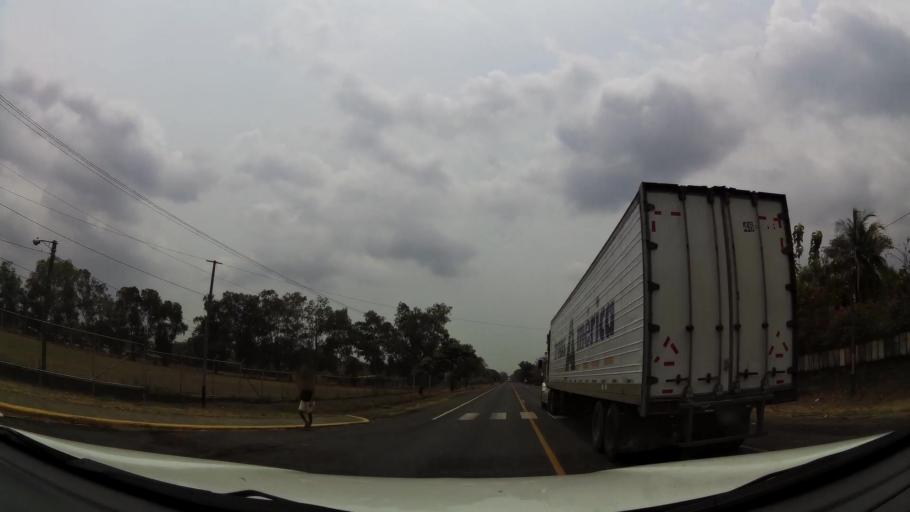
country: NI
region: Leon
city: Telica
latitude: 12.5242
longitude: -86.8744
